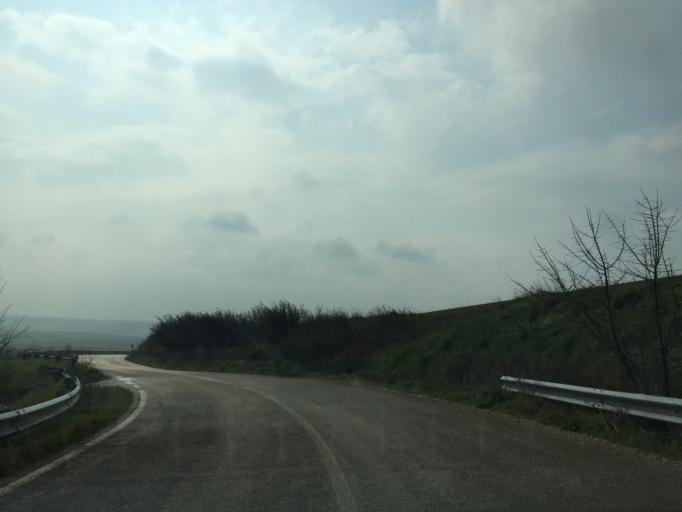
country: IT
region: Apulia
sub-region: Provincia di Foggia
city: Troia
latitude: 41.3640
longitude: 15.3239
